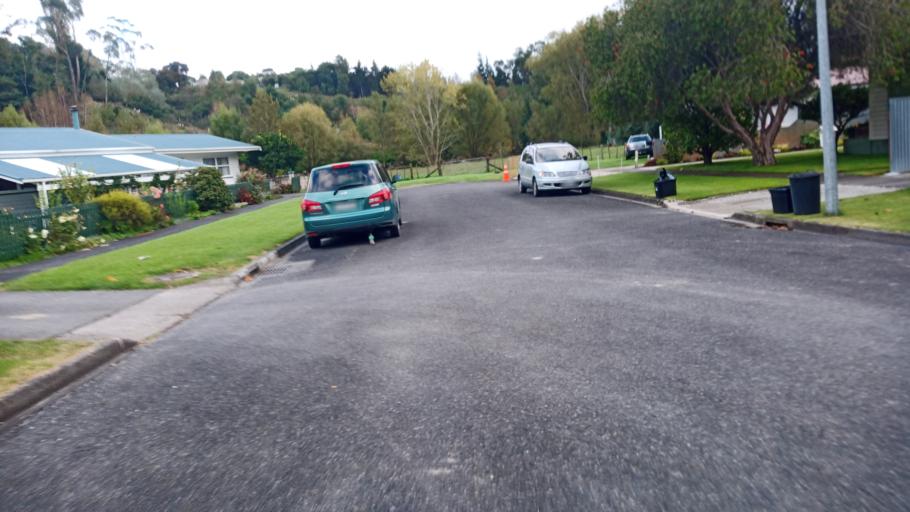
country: NZ
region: Gisborne
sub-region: Gisborne District
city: Gisborne
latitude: -38.6455
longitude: 178.0246
